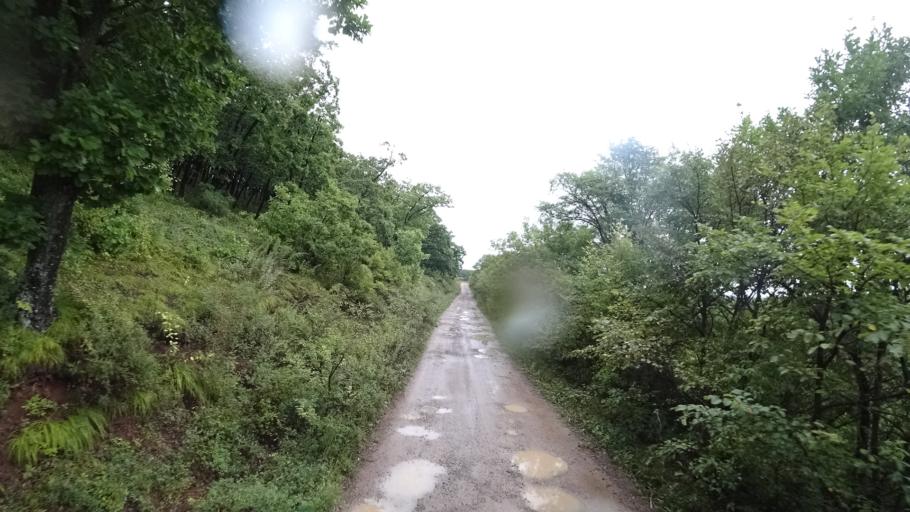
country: RU
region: Primorskiy
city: Monastyrishche
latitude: 44.2604
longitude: 132.4074
